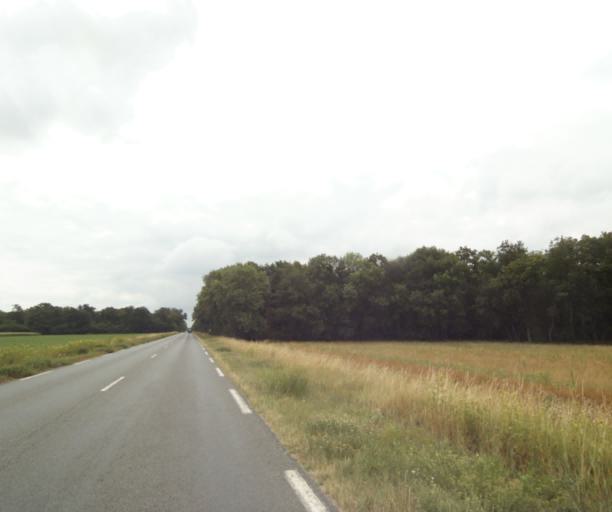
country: FR
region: Centre
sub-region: Departement du Loiret
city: Darvoy
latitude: 47.8800
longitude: 2.0956
